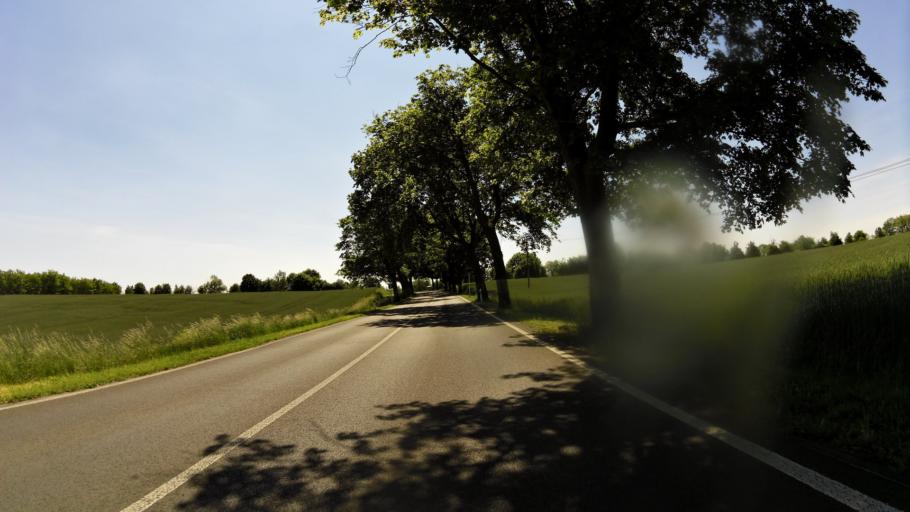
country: DE
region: Brandenburg
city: Lebus
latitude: 52.4028
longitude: 14.5188
